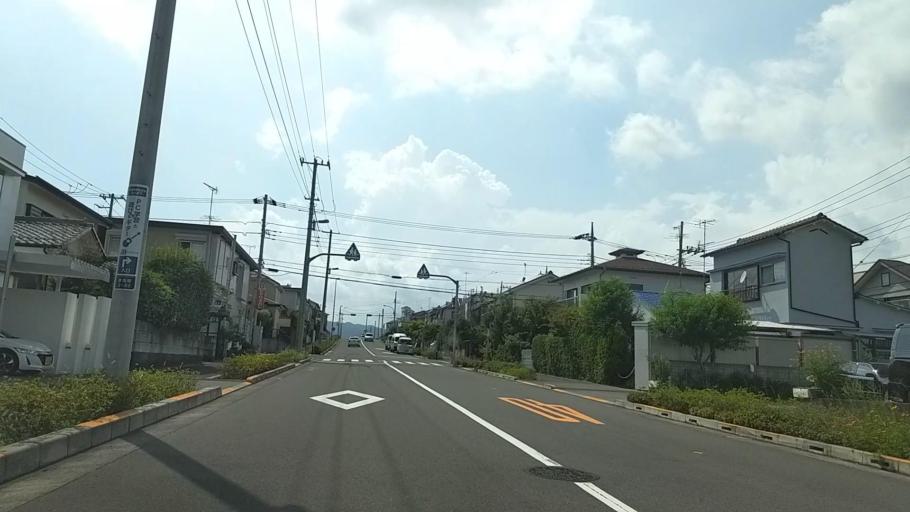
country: JP
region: Tokyo
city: Hachioji
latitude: 35.6488
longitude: 139.3152
